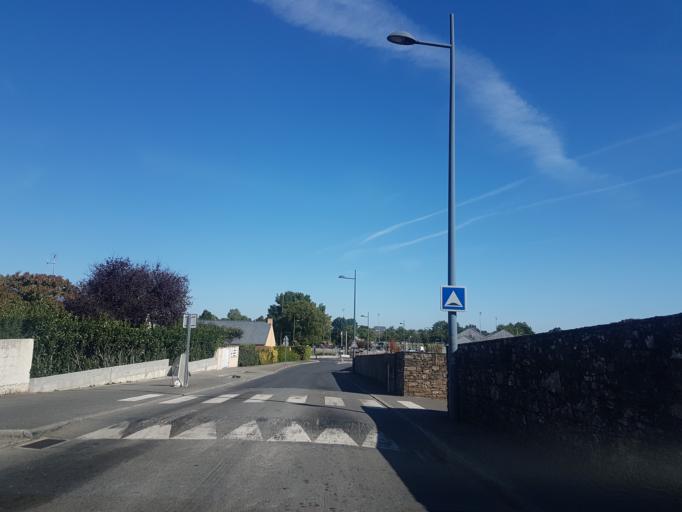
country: FR
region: Pays de la Loire
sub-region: Departement de la Loire-Atlantique
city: Petit-Mars
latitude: 47.3968
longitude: -1.4540
